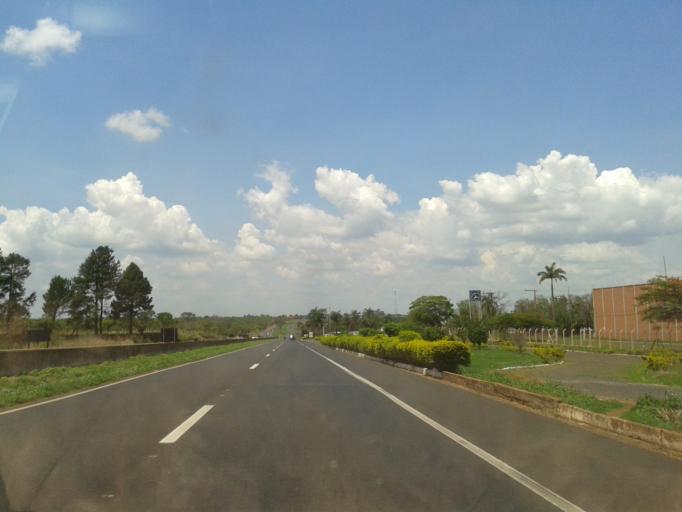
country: BR
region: Minas Gerais
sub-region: Araguari
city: Araguari
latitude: -18.6783
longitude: -48.1786
